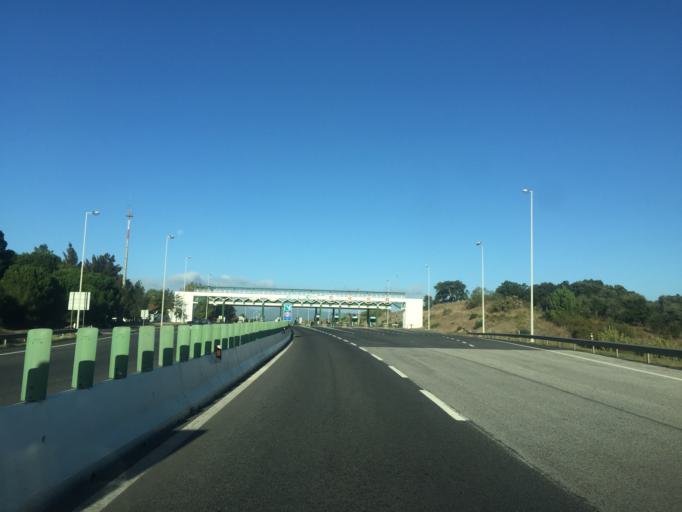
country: PT
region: Lisbon
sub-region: Azambuja
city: Aveiras de Cima
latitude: 39.1424
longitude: -8.8903
